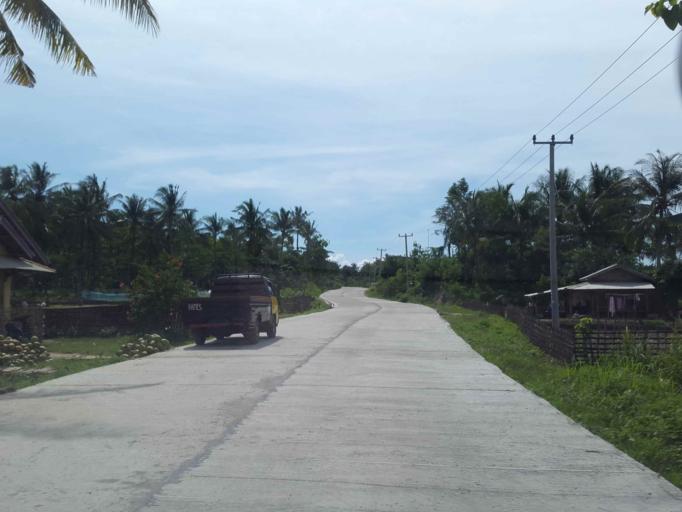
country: ID
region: Banten
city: Citeureup
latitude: -6.4976
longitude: 105.6528
